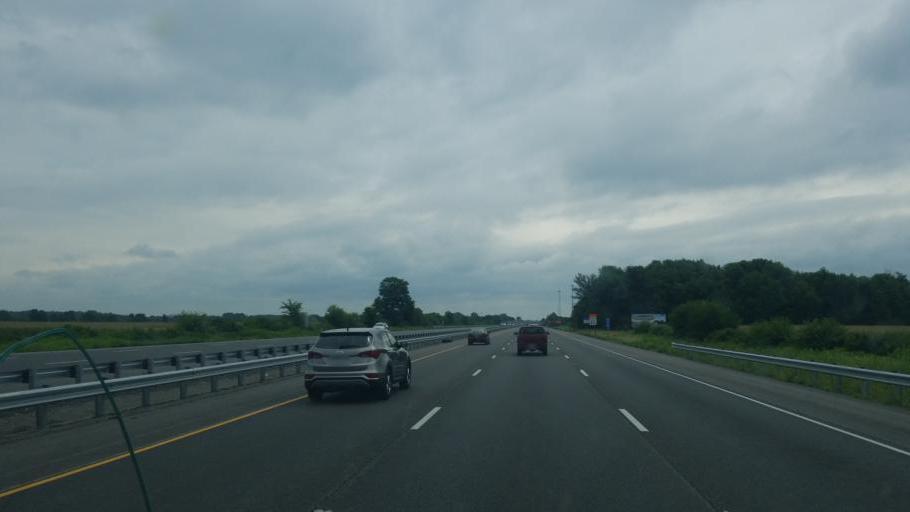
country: US
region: Indiana
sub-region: Madison County
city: Ingalls
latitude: 39.9914
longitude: -85.8080
